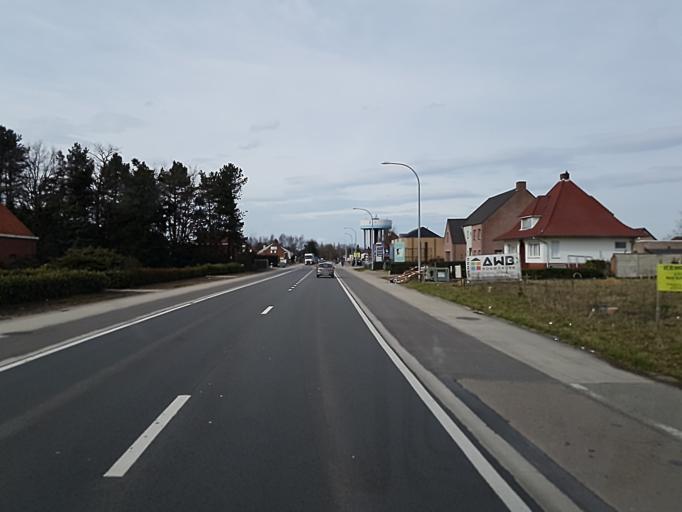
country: BE
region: Flanders
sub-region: Provincie Antwerpen
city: Dessel
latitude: 51.2477
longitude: 5.1083
